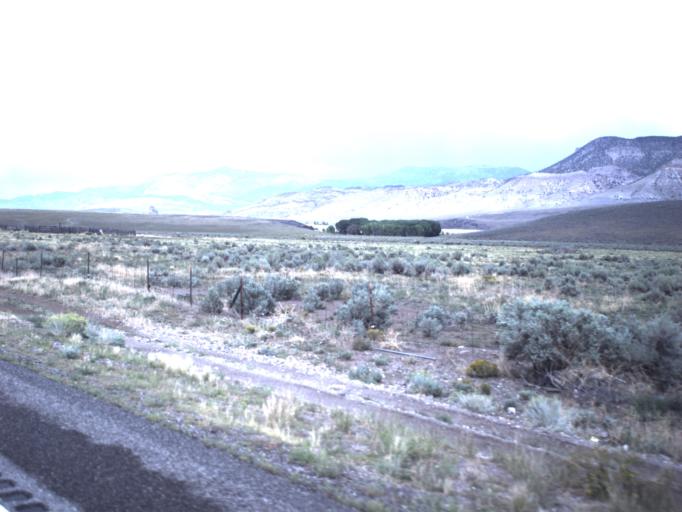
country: US
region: Utah
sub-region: Piute County
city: Junction
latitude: 38.2607
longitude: -112.2209
